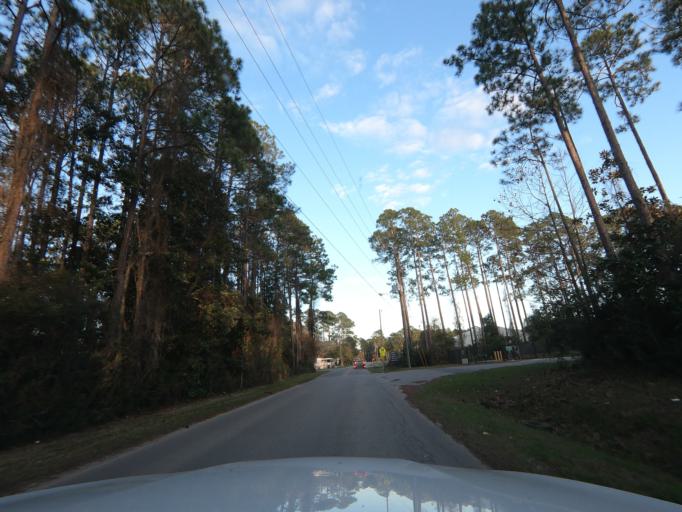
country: US
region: Florida
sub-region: Bay County
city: Laguna Beach
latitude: 30.2893
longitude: -85.8608
